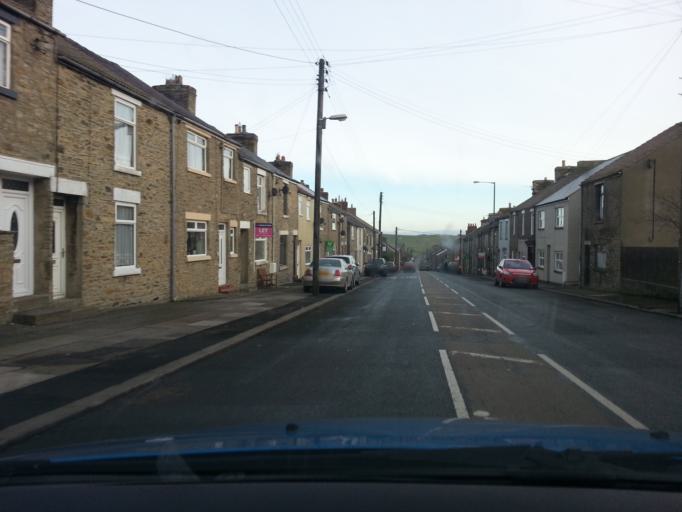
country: GB
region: England
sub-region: County Durham
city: Tow Law
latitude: 54.7407
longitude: -1.7833
